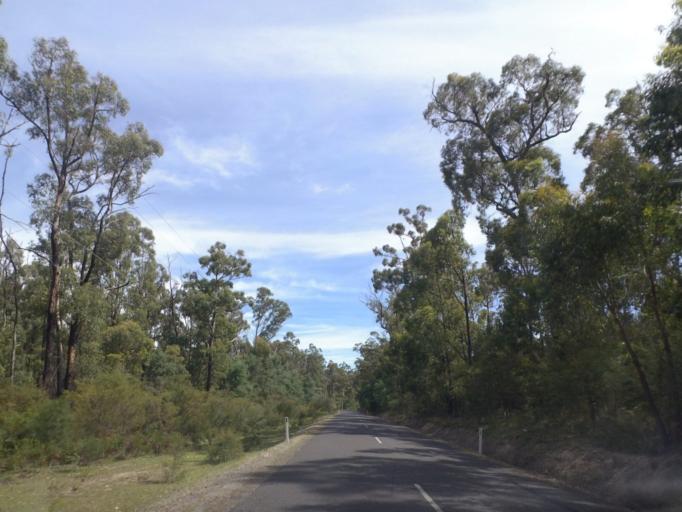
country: AU
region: Victoria
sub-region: Murrindindi
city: Kinglake West
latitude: -37.4721
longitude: 145.3944
